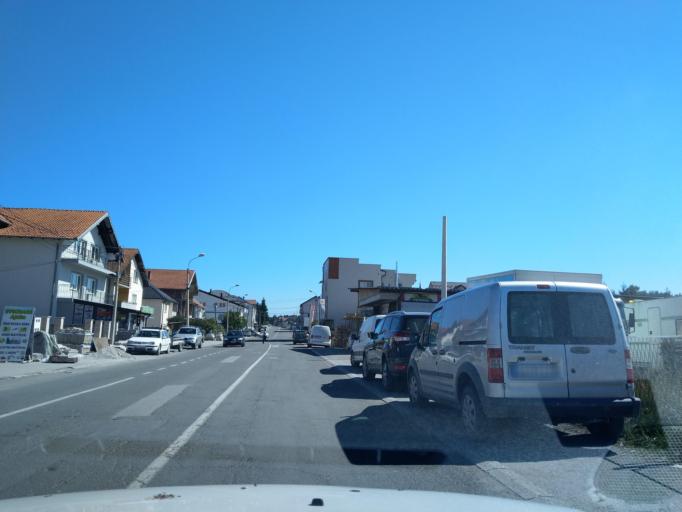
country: RS
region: Central Serbia
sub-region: Zlatiborski Okrug
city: Sjenica
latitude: 43.2740
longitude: 20.0068
